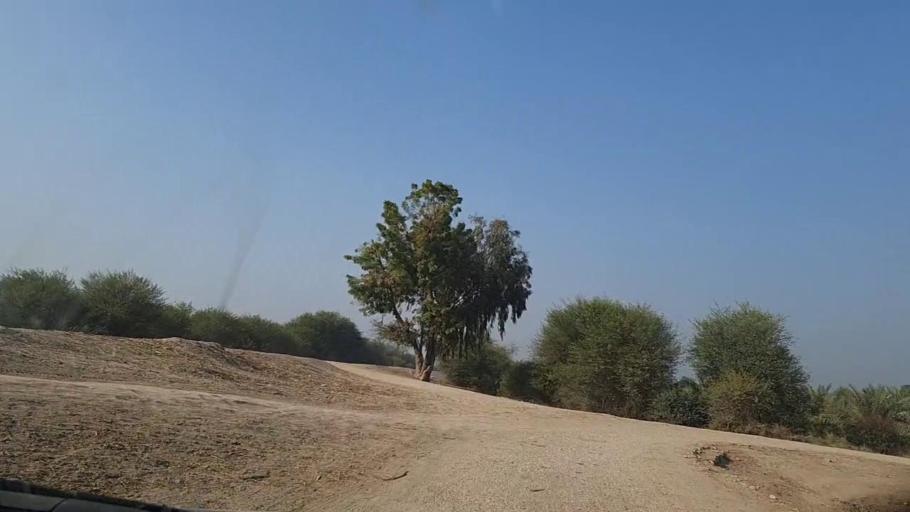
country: PK
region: Sindh
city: Moro
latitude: 26.8144
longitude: 67.9554
